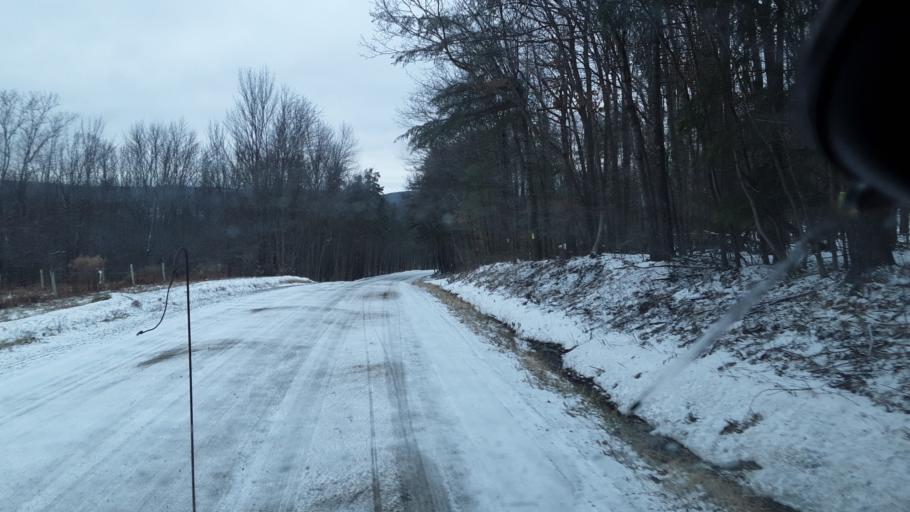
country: US
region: New York
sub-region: Allegany County
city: Friendship
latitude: 42.2820
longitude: -78.1622
